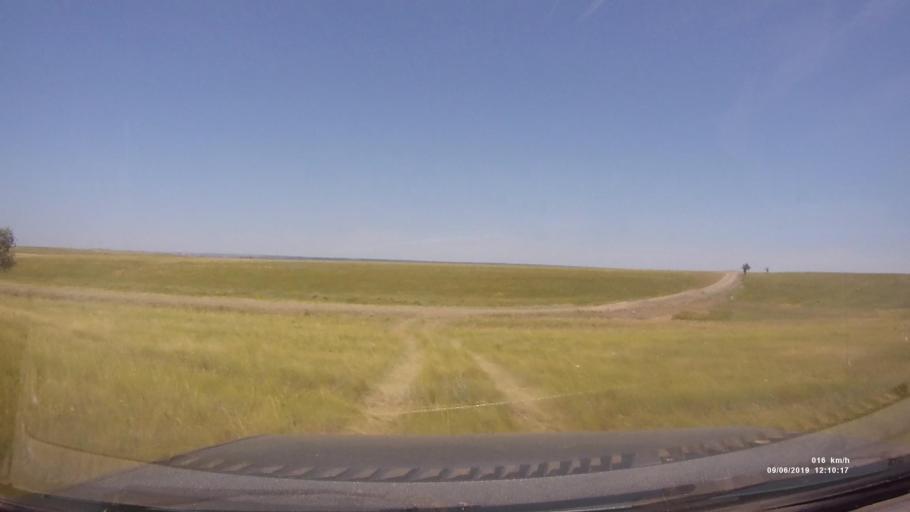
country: RU
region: Rostov
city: Staraya Stanitsa
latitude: 48.2500
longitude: 40.3390
